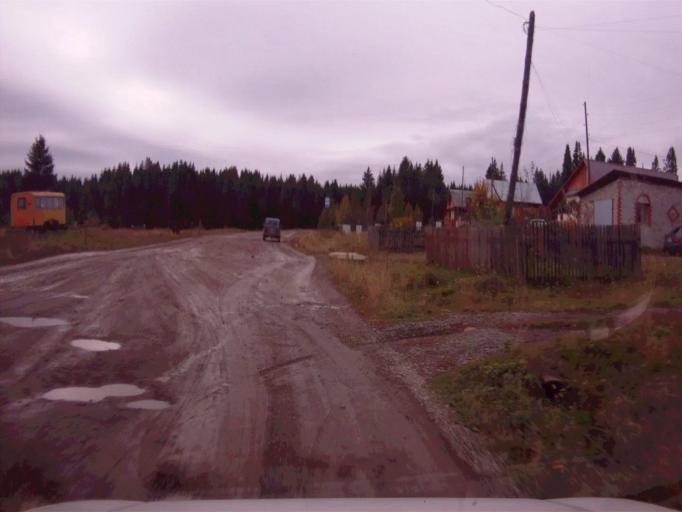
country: RU
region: Chelyabinsk
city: Nyazepetrovsk
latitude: 56.0642
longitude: 59.5695
